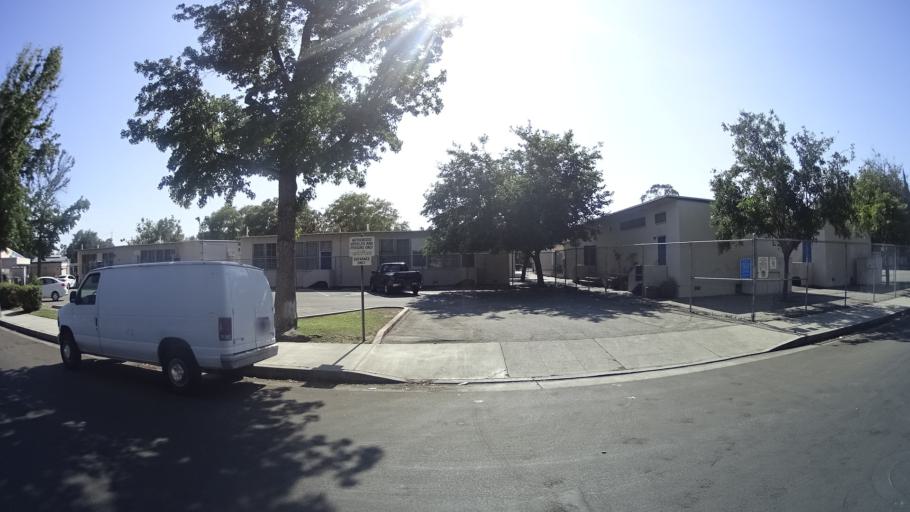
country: US
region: California
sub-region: Los Angeles County
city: Van Nuys
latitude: 34.1916
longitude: -118.4290
